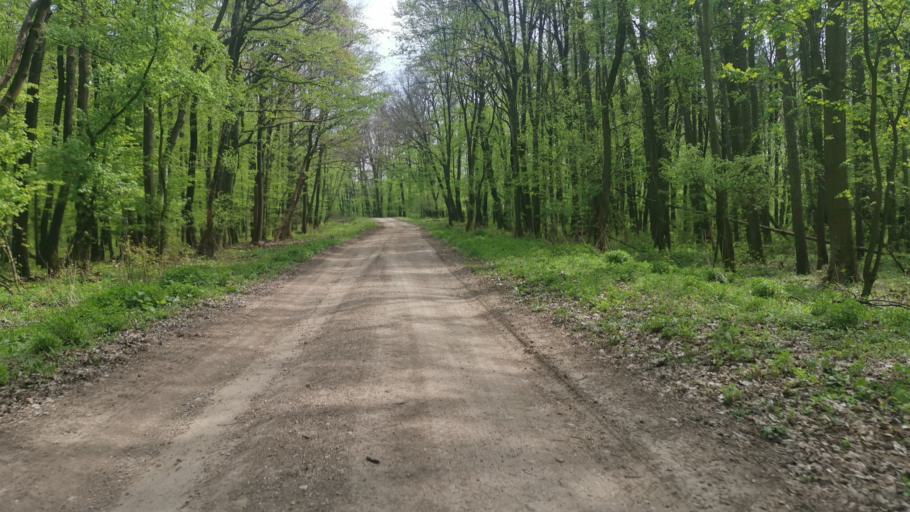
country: SK
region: Trnavsky
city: Smolenice
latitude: 48.5536
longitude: 17.4383
